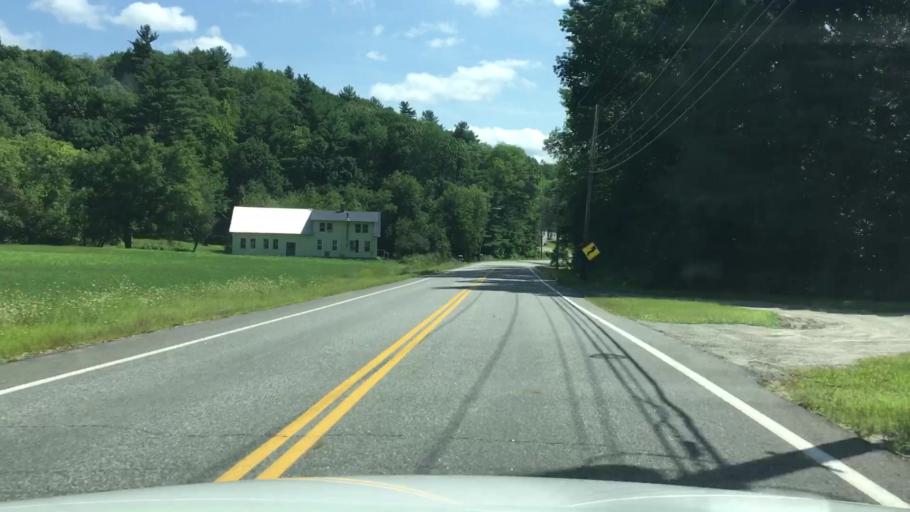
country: US
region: Maine
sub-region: Kennebec County
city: Augusta
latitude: 44.3361
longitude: -69.8048
